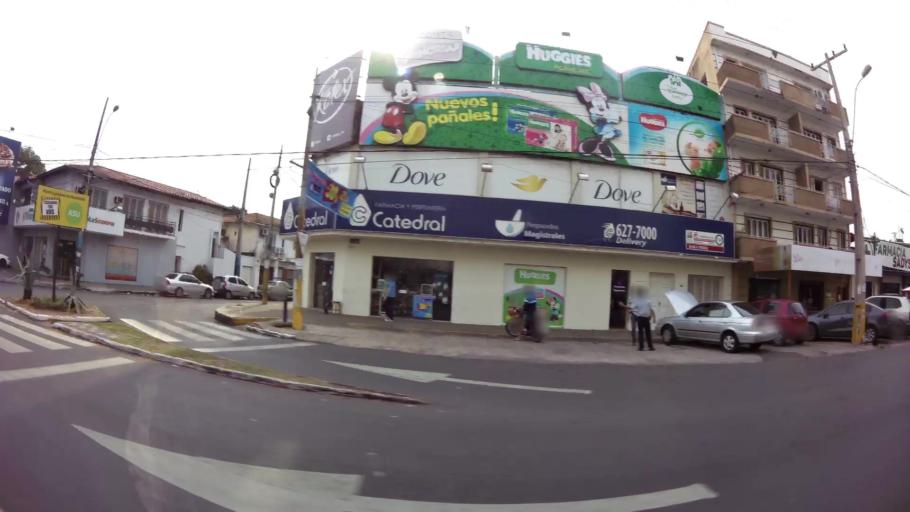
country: PY
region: Asuncion
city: Asuncion
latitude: -25.3007
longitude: -57.6132
